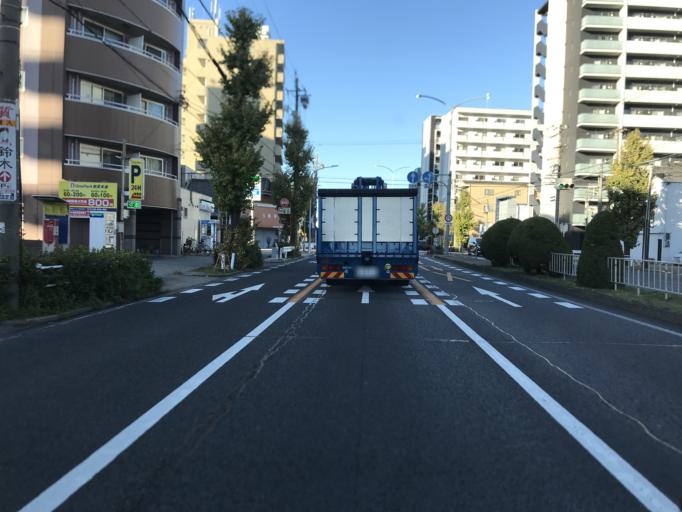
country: JP
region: Aichi
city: Nagoya-shi
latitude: 35.1698
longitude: 136.8727
